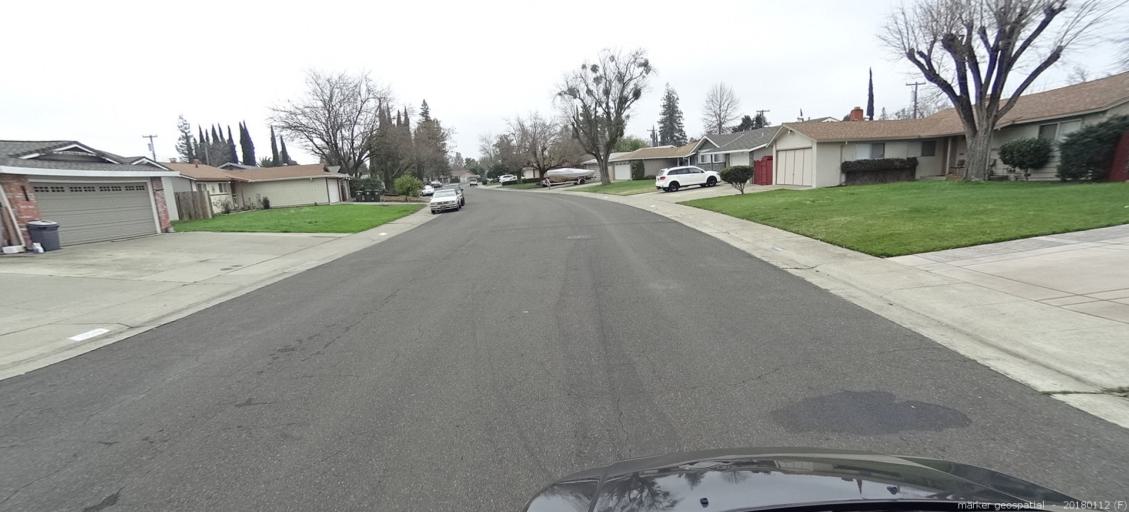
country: US
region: California
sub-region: Sacramento County
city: Rancho Cordova
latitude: 38.6085
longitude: -121.2888
